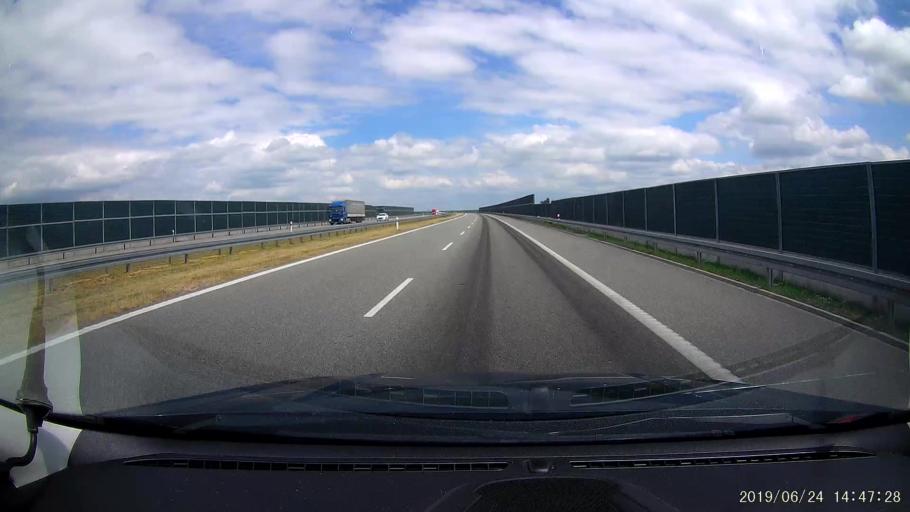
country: PL
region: Subcarpathian Voivodeship
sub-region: Powiat debicki
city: Zyrakow
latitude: 50.0792
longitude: 21.3953
